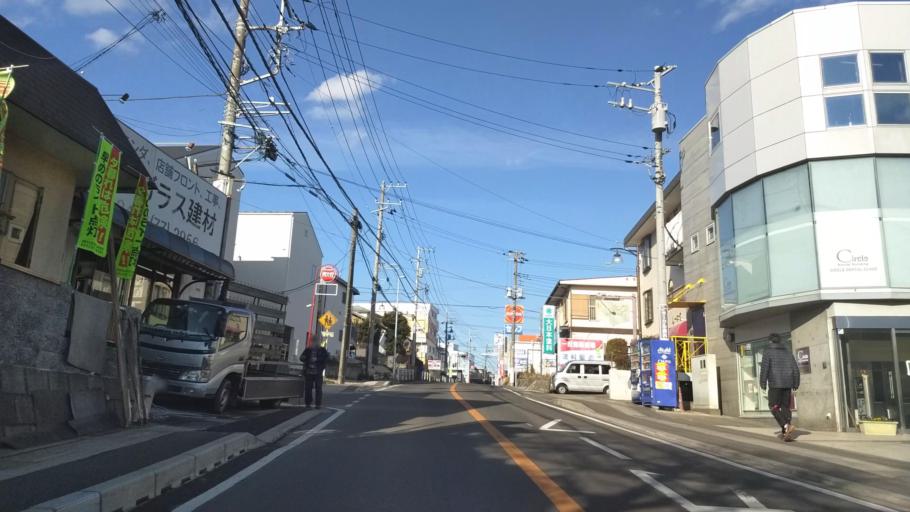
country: JP
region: Kanagawa
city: Isehara
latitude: 35.3744
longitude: 139.2762
